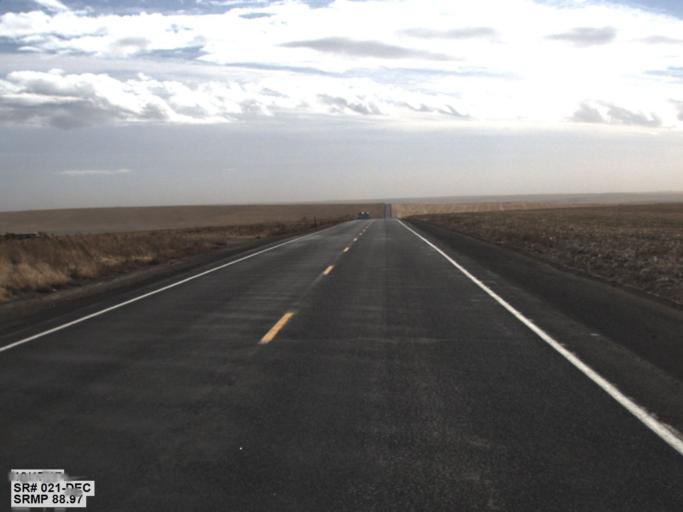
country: US
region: Washington
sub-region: Okanogan County
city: Coulee Dam
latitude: 47.7265
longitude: -118.7220
